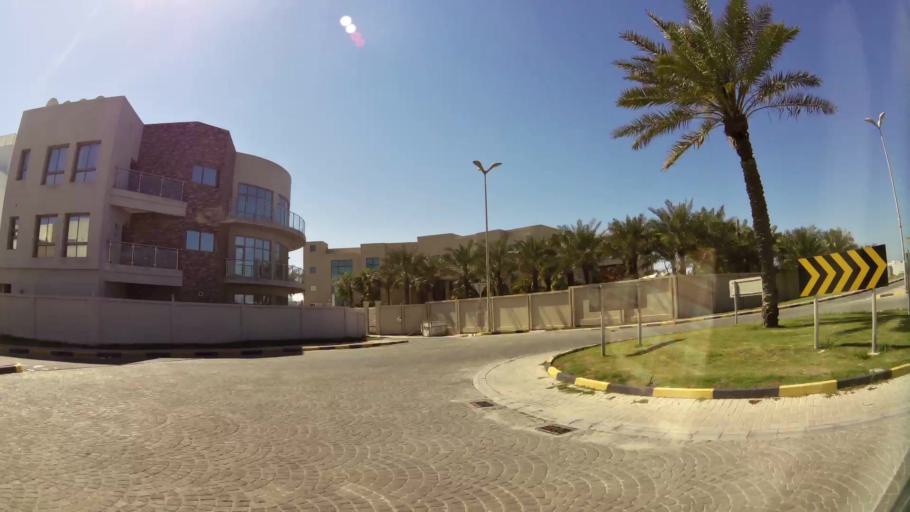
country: BH
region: Muharraq
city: Al Hadd
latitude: 26.2922
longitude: 50.6740
